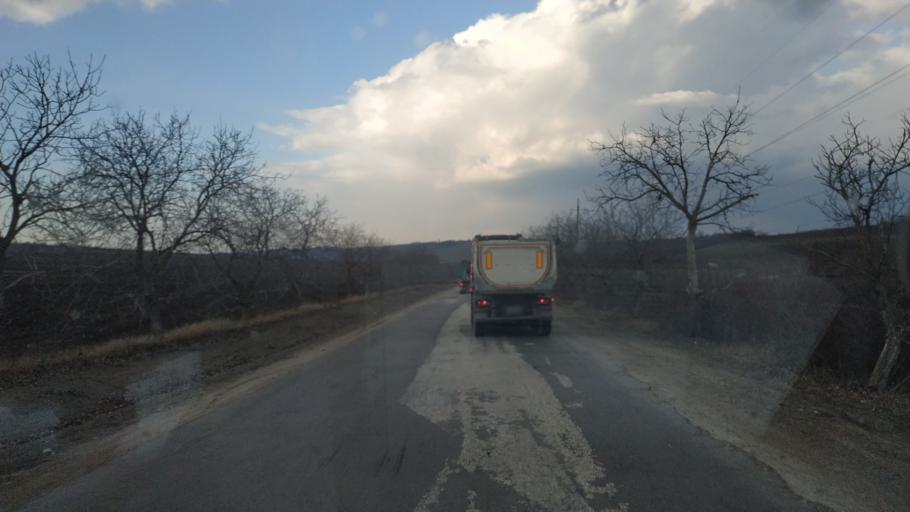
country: MD
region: Anenii Noi
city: Anenii Noi
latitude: 46.9758
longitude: 29.2850
